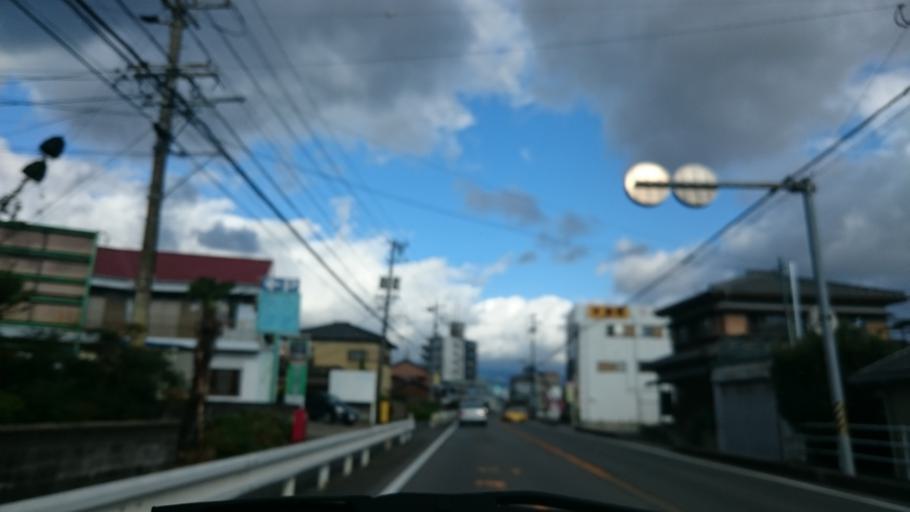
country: JP
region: Mie
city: Komono
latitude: 35.0090
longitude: 136.5200
